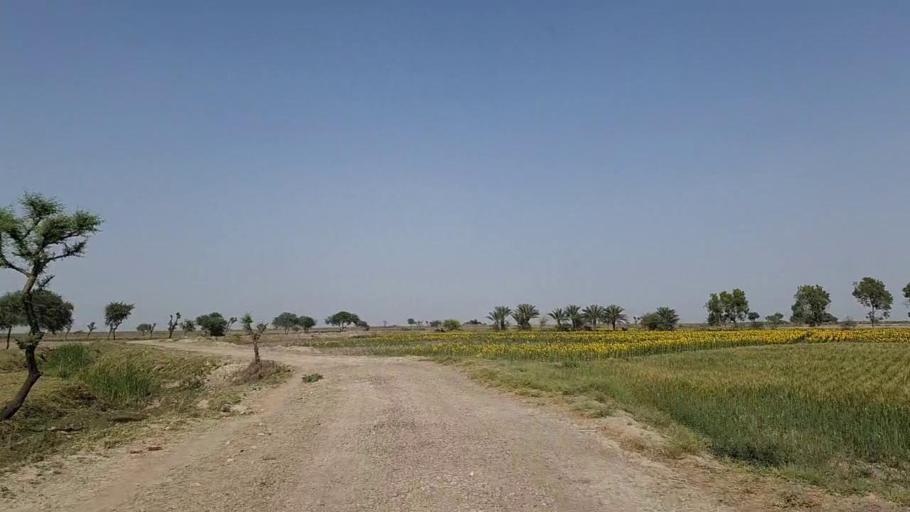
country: PK
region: Sindh
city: Jati
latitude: 24.3504
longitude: 68.3140
